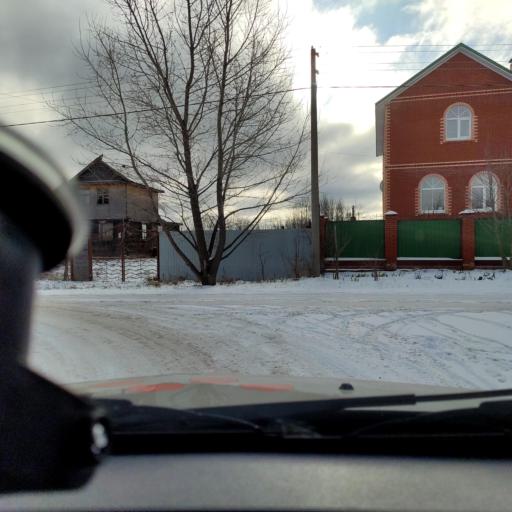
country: RU
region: Bashkortostan
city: Avdon
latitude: 54.7849
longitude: 55.7213
